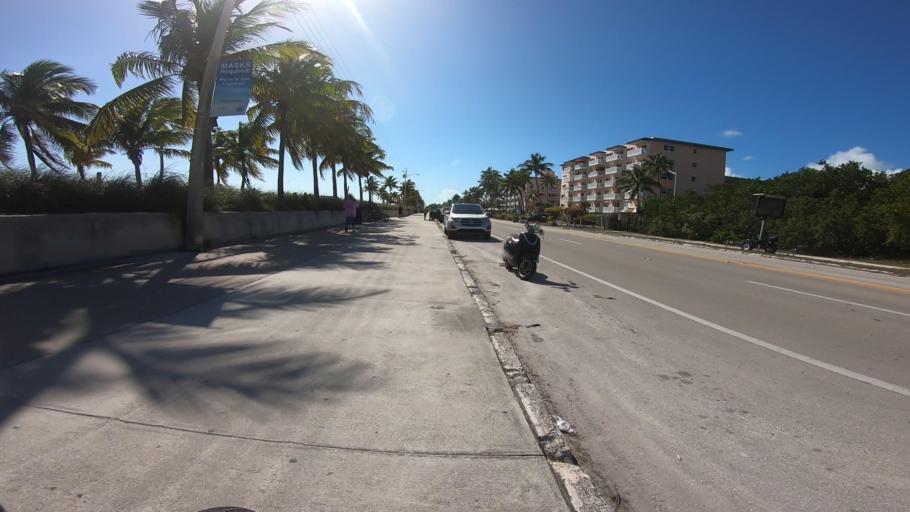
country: US
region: Florida
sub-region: Monroe County
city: Key West
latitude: 24.5520
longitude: -81.7694
